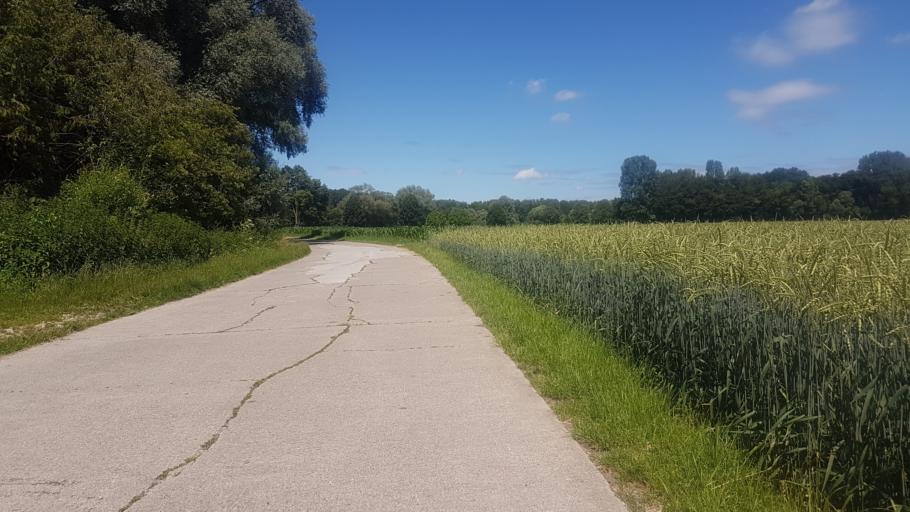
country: DE
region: Bavaria
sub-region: Swabia
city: Blindheim
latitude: 48.6187
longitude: 10.6015
